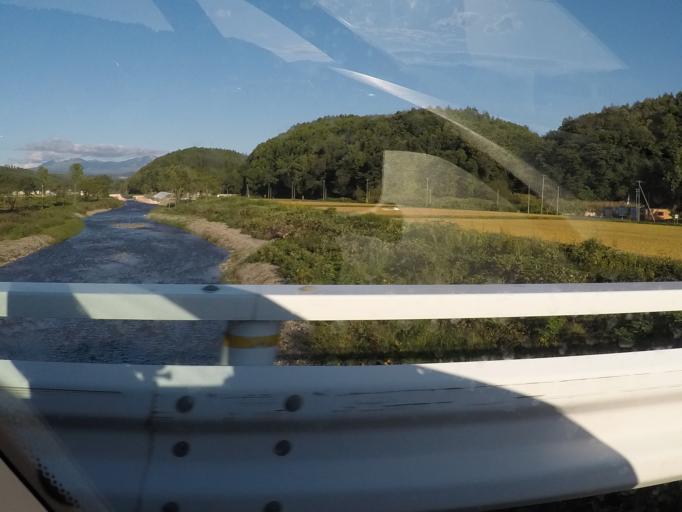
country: JP
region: Hokkaido
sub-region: Asahikawa-shi
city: Asahikawa
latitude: 43.6226
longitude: 142.5018
